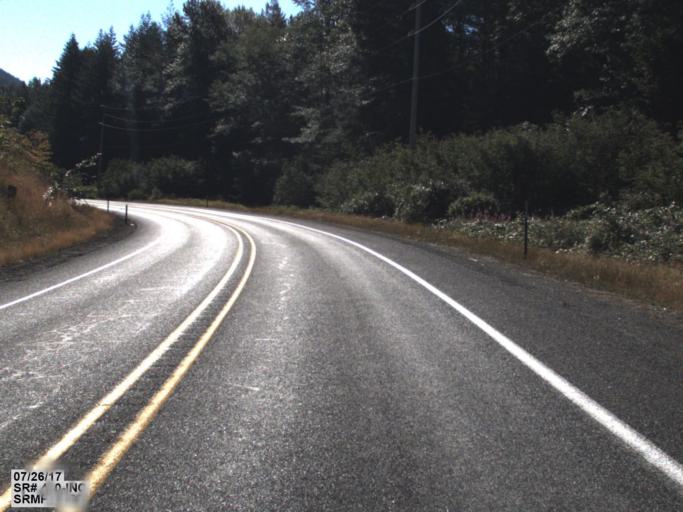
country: US
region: Washington
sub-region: King County
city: Enumclaw
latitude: 47.1647
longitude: -121.7542
